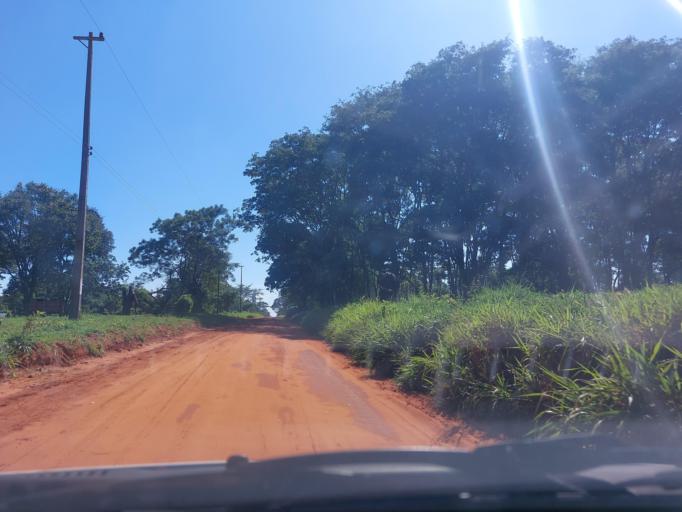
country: PY
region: San Pedro
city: Lima
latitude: -24.1559
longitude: -56.0114
